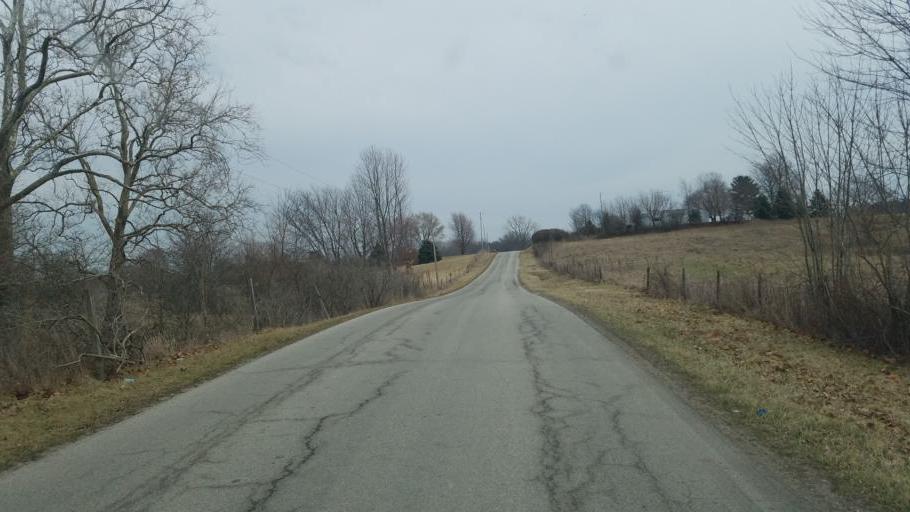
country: US
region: Ohio
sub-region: Crawford County
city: Galion
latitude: 40.7124
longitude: -82.8085
